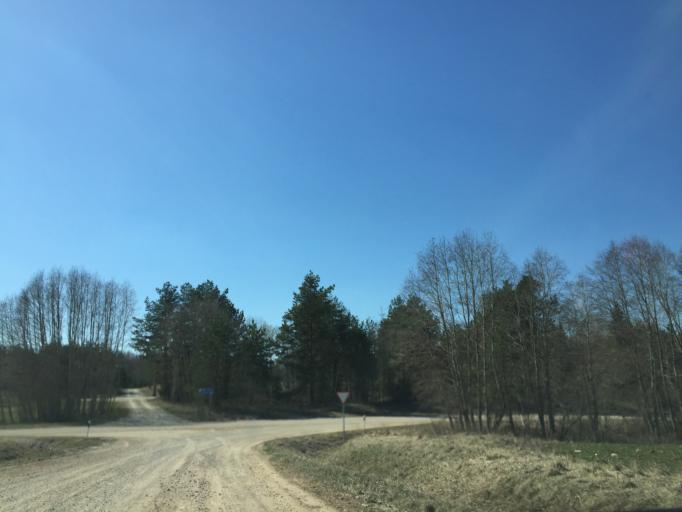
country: EE
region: Viljandimaa
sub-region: Viiratsi vald
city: Viiratsi
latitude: 58.3138
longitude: 25.6863
